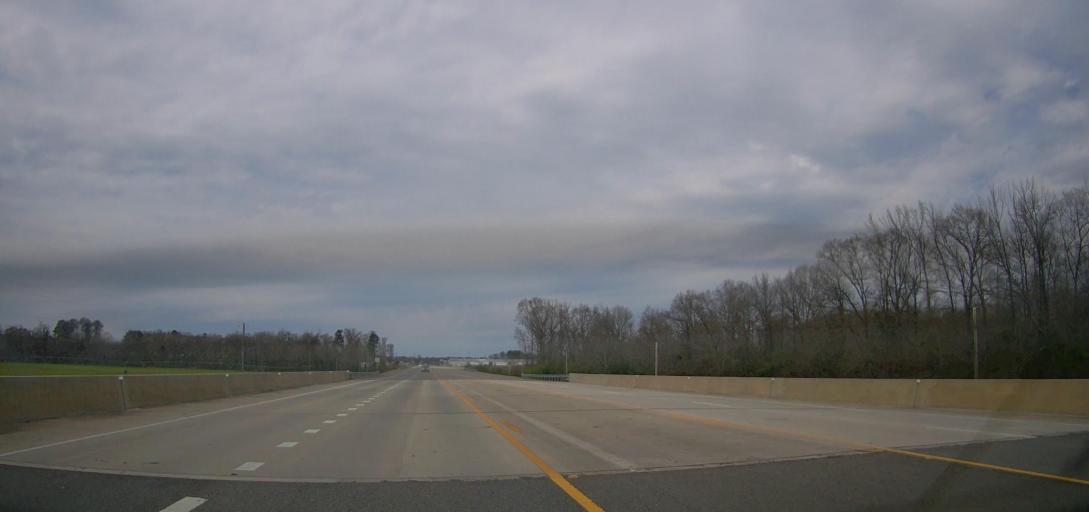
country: US
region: Alabama
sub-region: Marion County
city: Hamilton
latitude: 34.1029
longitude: -87.9891
